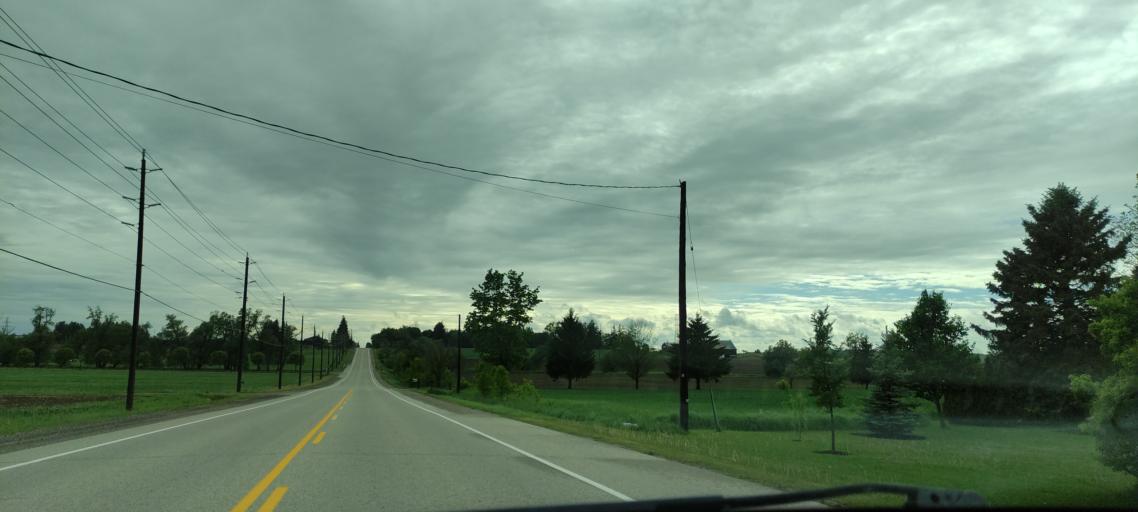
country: CA
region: Ontario
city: Kitchener
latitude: 43.3822
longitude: -80.6508
